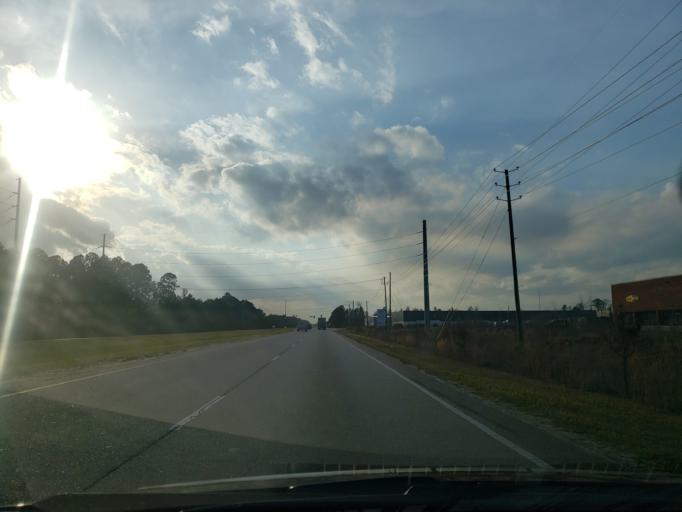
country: US
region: Georgia
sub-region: Chatham County
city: Pooler
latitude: 32.1630
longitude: -81.2392
